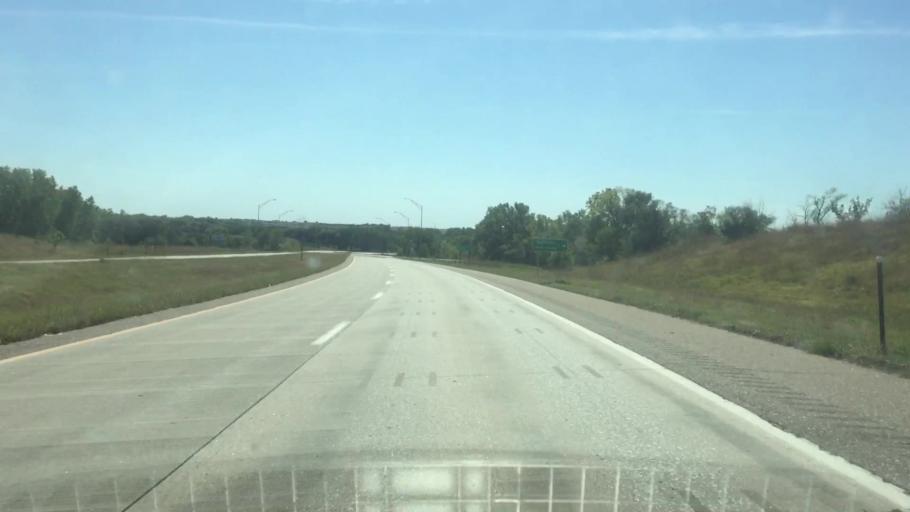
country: US
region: Nebraska
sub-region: Thayer County
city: Hebron
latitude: 40.1696
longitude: -97.5743
